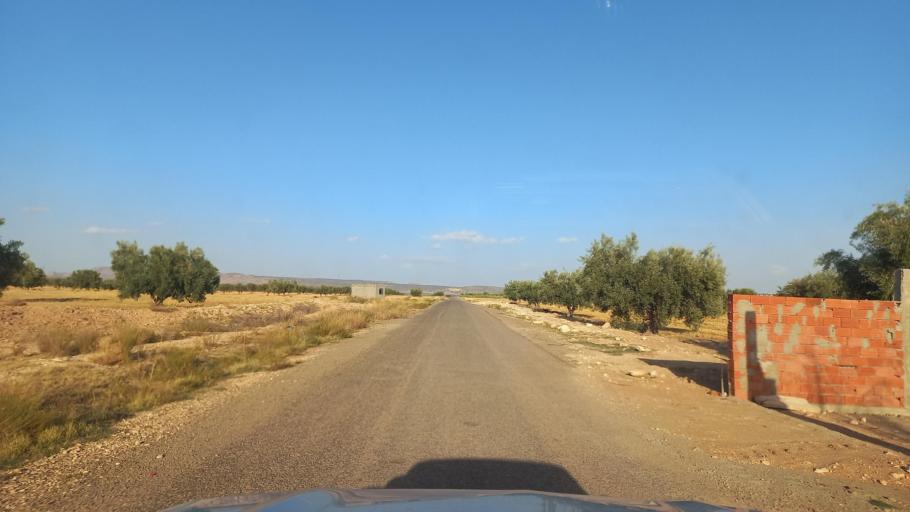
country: TN
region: Al Qasrayn
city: Kasserine
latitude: 35.2868
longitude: 9.0305
